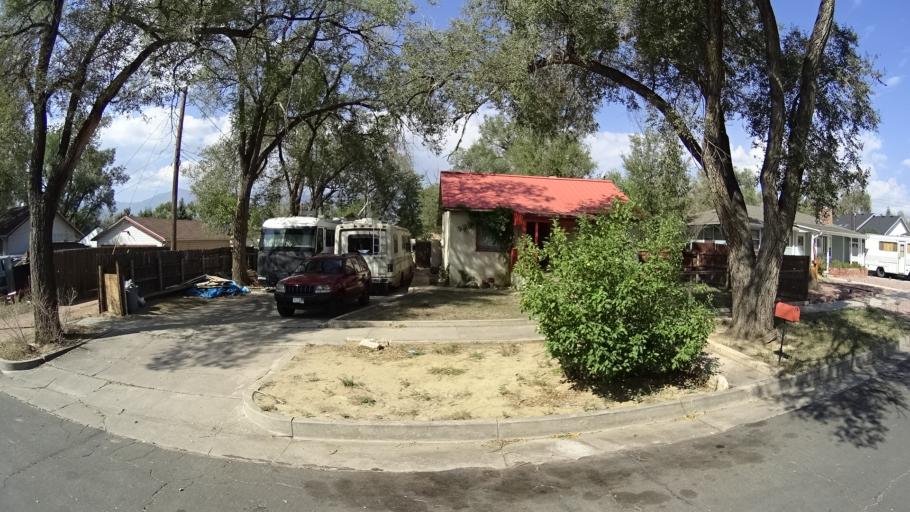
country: US
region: Colorado
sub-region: El Paso County
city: Colorado Springs
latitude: 38.8231
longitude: -104.8013
